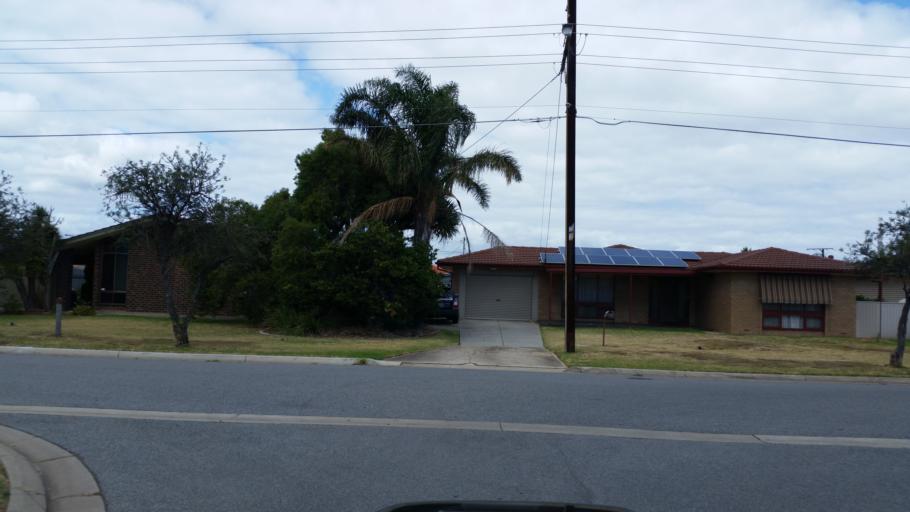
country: AU
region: South Australia
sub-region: Charles Sturt
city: Seaton
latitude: -34.9012
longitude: 138.5085
